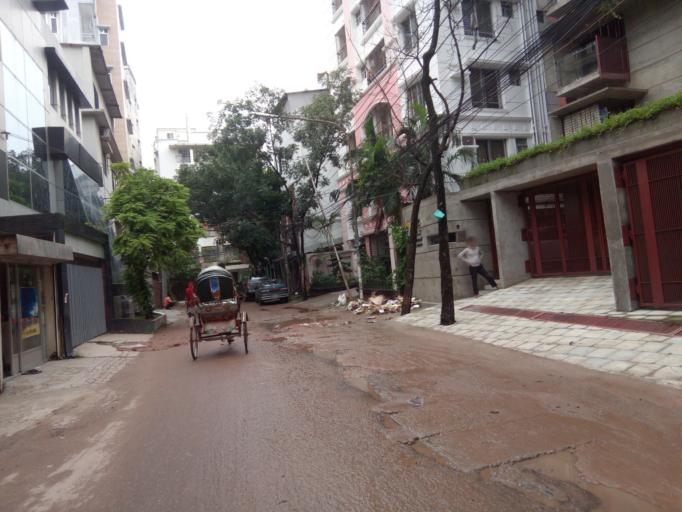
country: BD
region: Dhaka
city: Azimpur
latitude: 23.7540
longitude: 90.3691
